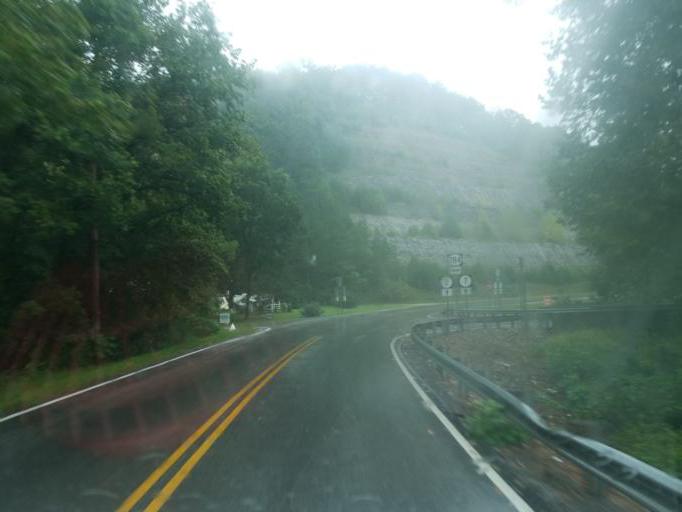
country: US
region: Kentucky
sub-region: Carter County
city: Grayson
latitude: 38.4676
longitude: -83.0502
